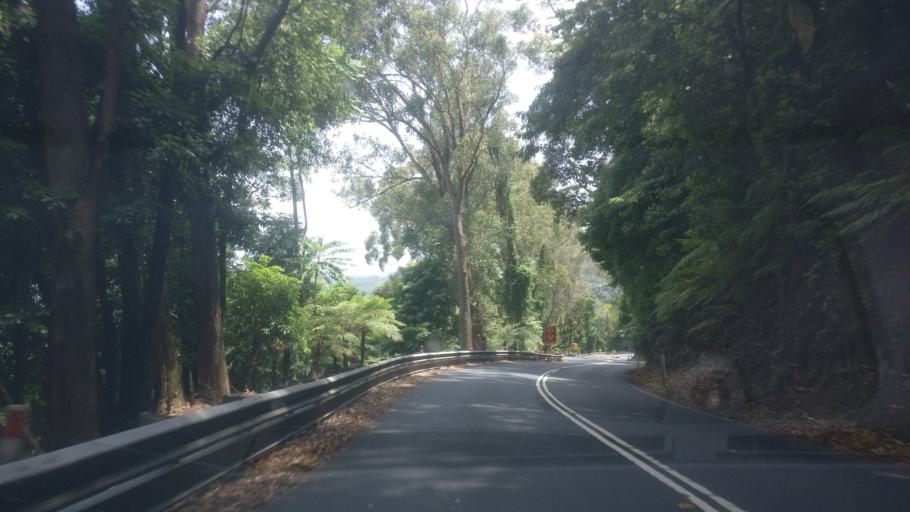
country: AU
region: New South Wales
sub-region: Shoalhaven Shire
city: Kangaroo Valley
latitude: -34.7904
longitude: 150.5612
